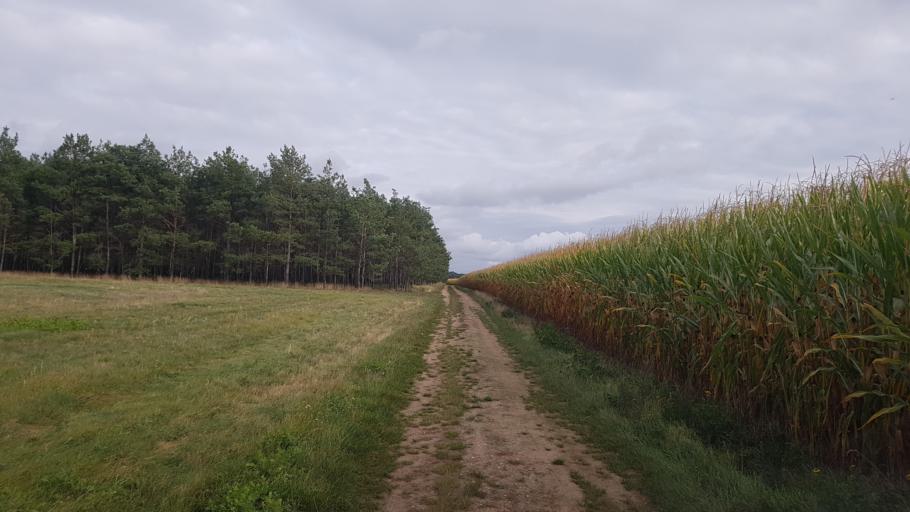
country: DE
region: Saxony
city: Nauwalde
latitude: 51.4731
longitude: 13.4422
